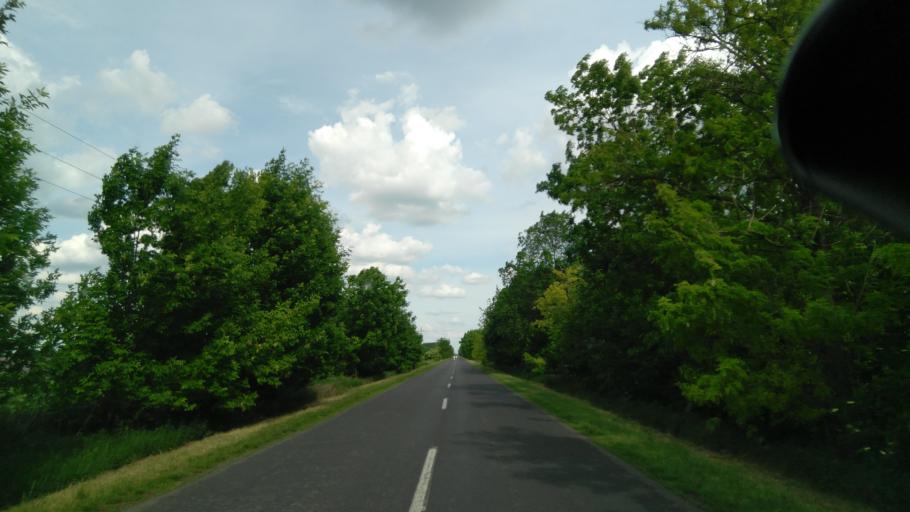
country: RO
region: Arad
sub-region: Comuna Peregu Mare
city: Peregu Mic
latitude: 46.2959
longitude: 20.9632
